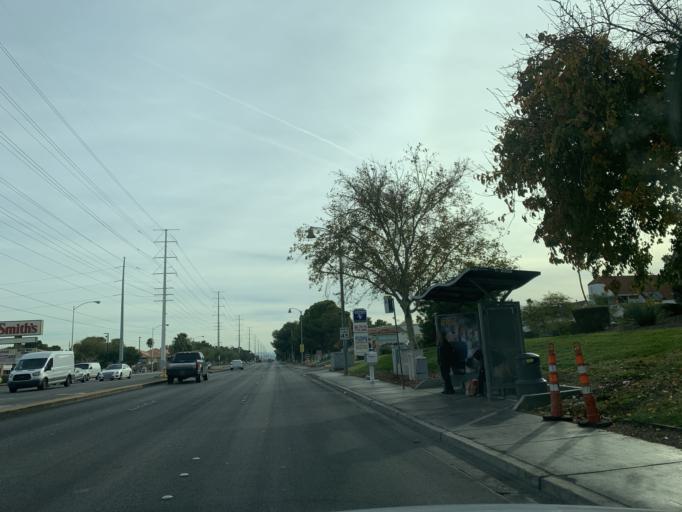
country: US
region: Nevada
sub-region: Clark County
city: Spring Valley
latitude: 36.1437
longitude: -115.2790
